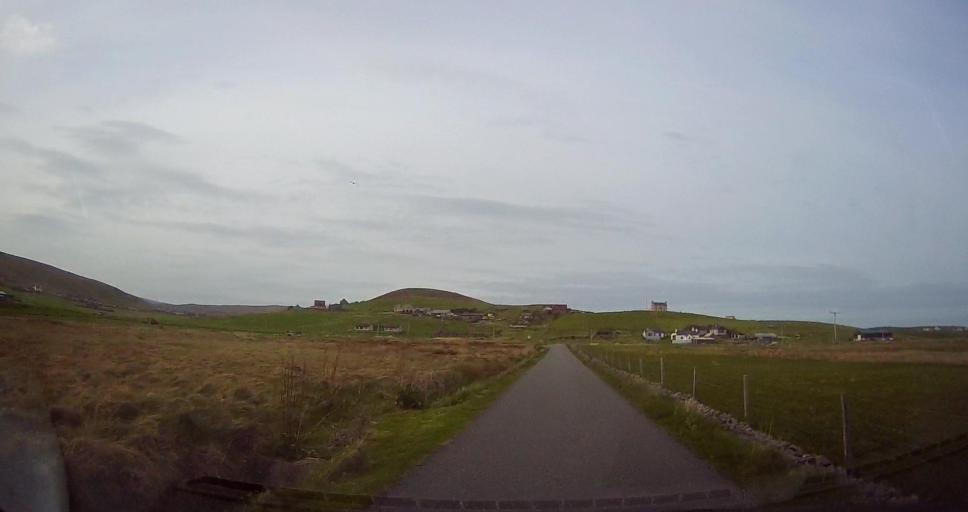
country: GB
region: Scotland
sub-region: Shetland Islands
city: Sandwick
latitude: 60.0447
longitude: -1.2168
